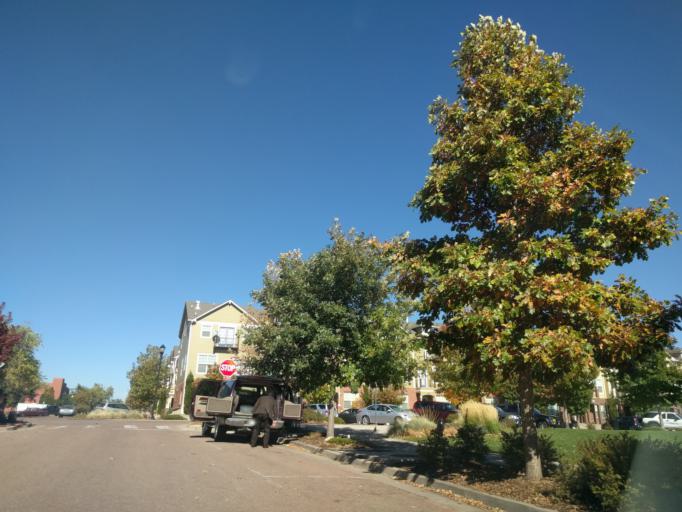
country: US
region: Colorado
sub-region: El Paso County
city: Colorado Springs
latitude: 38.8213
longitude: -104.8204
